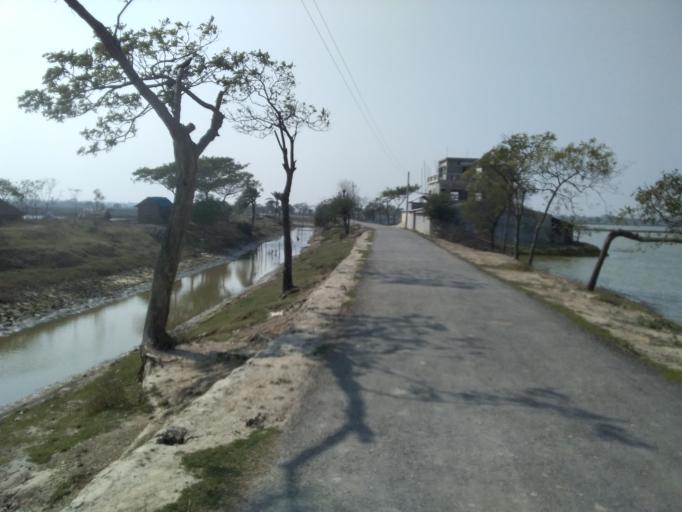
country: BD
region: Khulna
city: Satkhira
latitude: 22.6338
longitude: 89.0169
